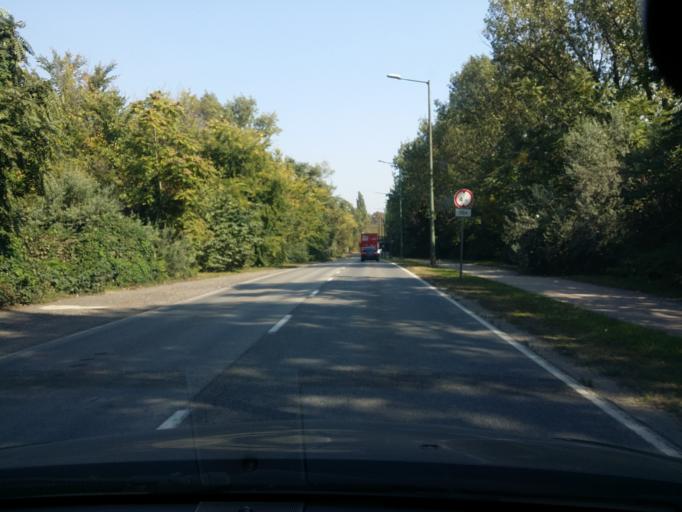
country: HU
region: Bacs-Kiskun
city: Dunavecse
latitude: 46.9320
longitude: 18.9466
